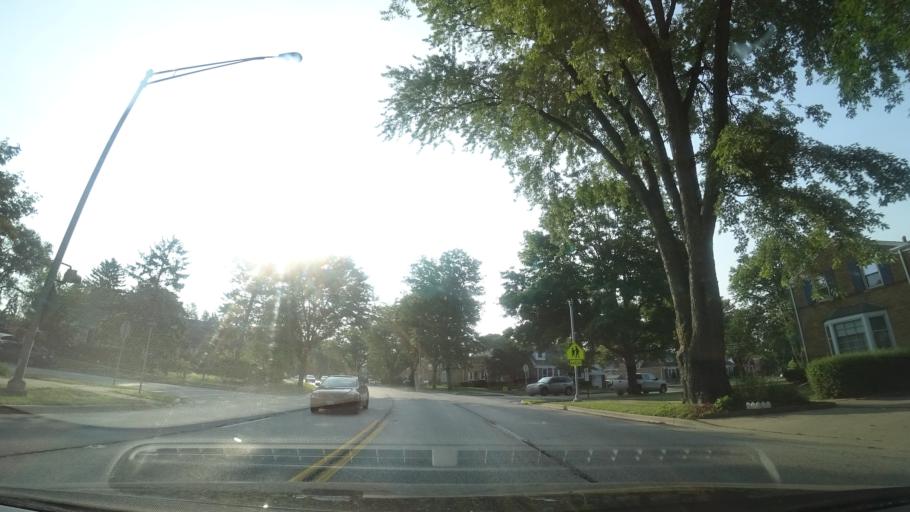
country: US
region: Illinois
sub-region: Cook County
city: Des Plaines
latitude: 42.0217
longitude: -87.8935
